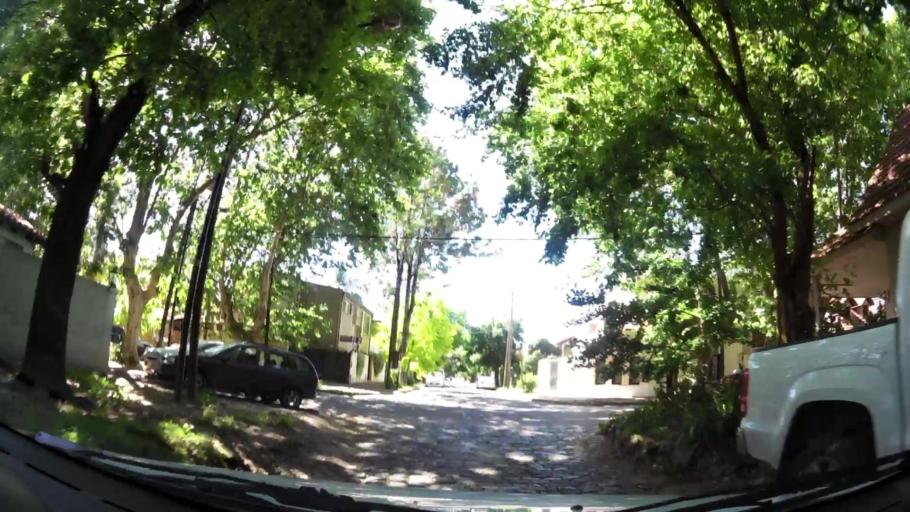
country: AR
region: Buenos Aires
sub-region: Partido de San Isidro
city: San Isidro
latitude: -34.4554
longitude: -58.5272
